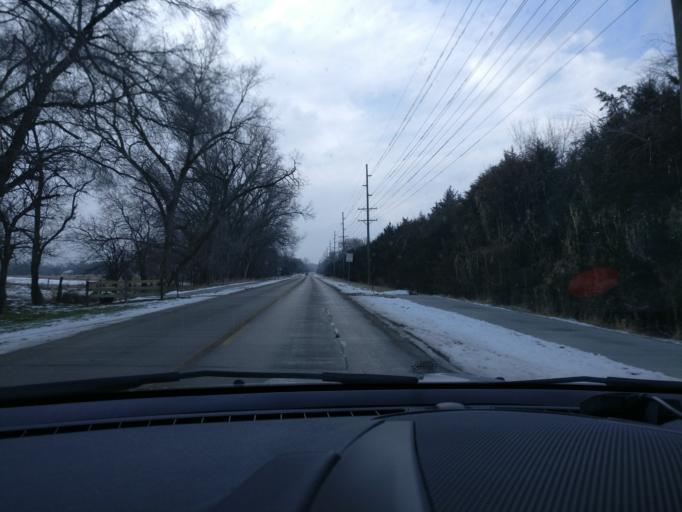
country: US
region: Nebraska
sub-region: Dodge County
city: Fremont
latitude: 41.4359
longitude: -96.5216
